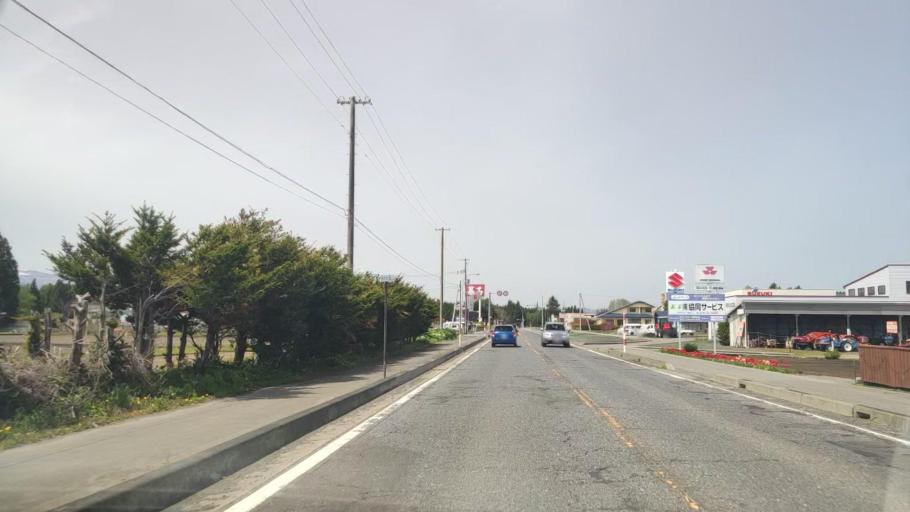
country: JP
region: Aomori
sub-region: Misawa Shi
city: Inuotose
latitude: 40.6750
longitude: 141.1766
